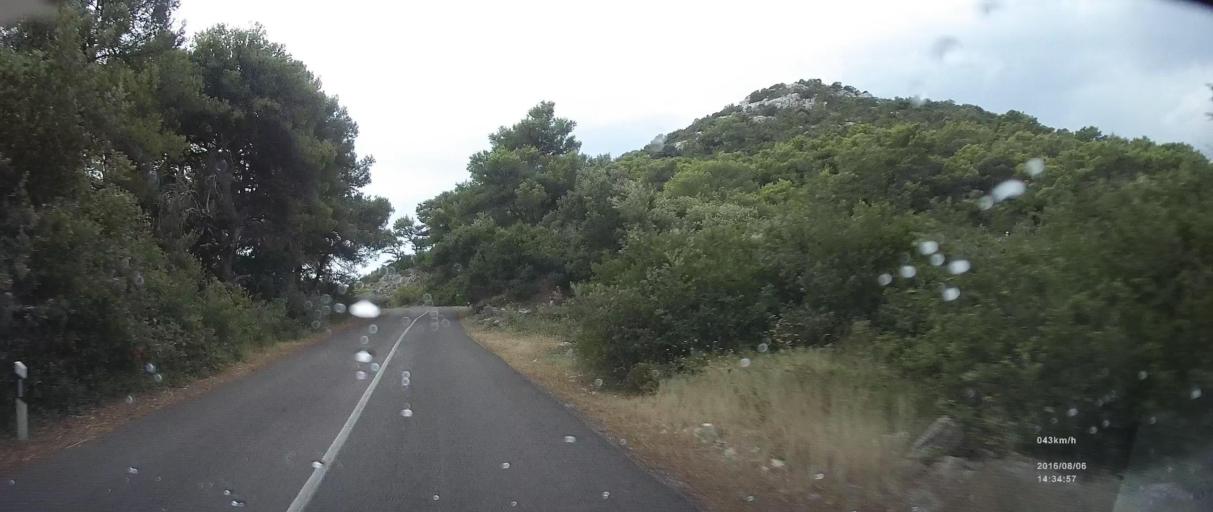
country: HR
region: Dubrovacko-Neretvanska
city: Ston
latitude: 42.7112
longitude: 17.6937
